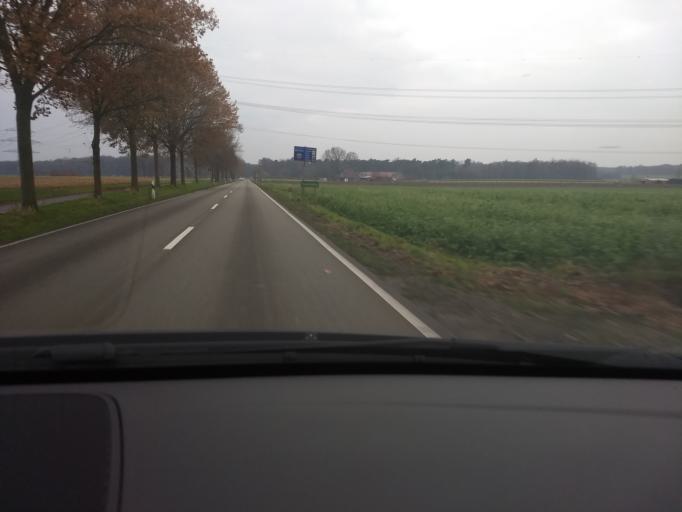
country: DE
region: North Rhine-Westphalia
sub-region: Regierungsbezirk Munster
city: Borken
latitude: 51.8677
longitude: 6.8973
